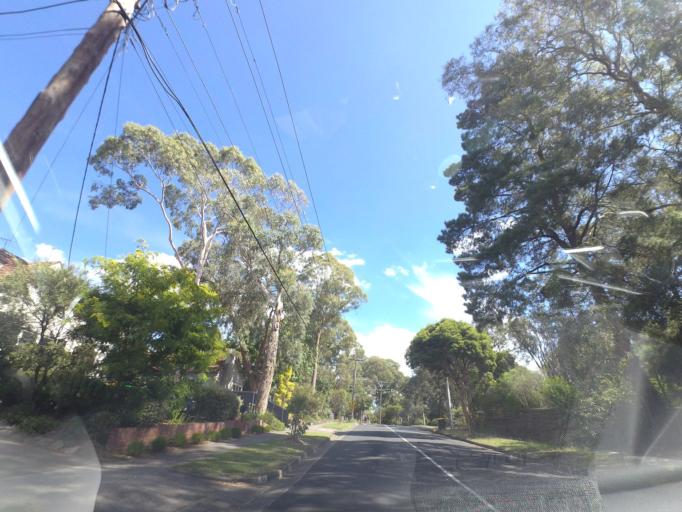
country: AU
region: Victoria
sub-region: Whitehorse
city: Blackburn
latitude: -37.8282
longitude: 145.1579
